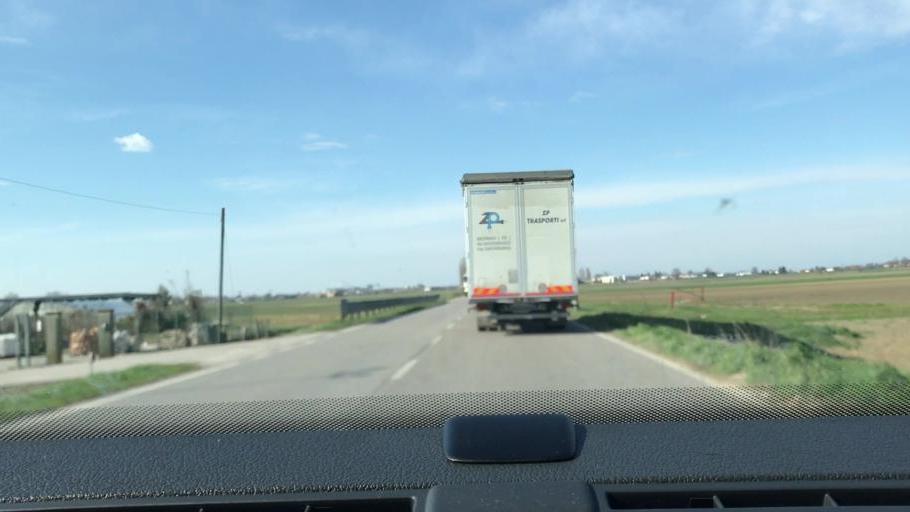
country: IT
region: Veneto
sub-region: Provincia di Rovigo
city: Calto
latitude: 45.0041
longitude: 11.3487
